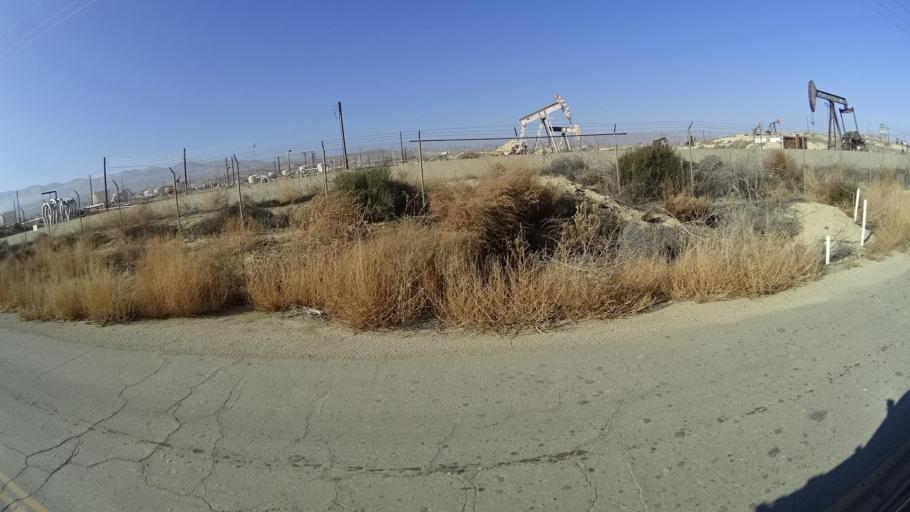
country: US
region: California
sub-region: Kern County
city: Taft Heights
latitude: 35.2159
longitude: -119.5982
